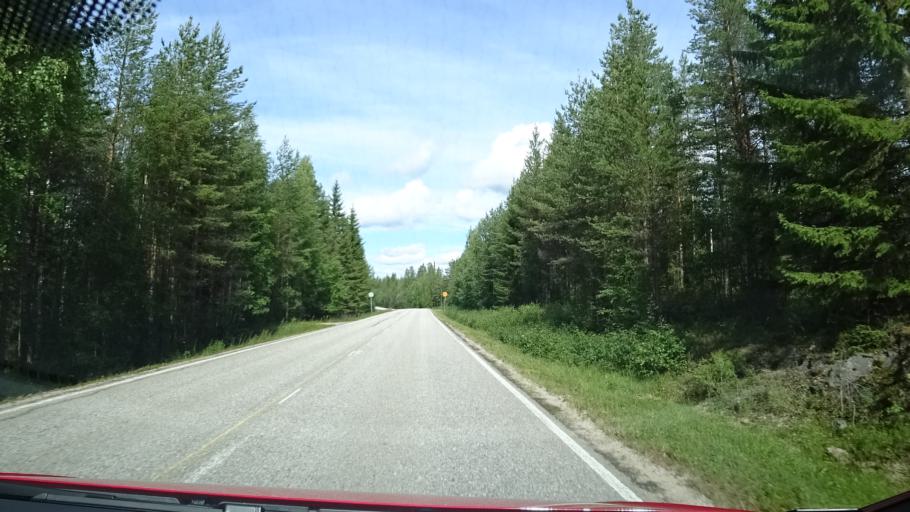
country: FI
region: Kainuu
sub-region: Kehys-Kainuu
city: Kuhmo
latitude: 64.4397
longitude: 29.8054
